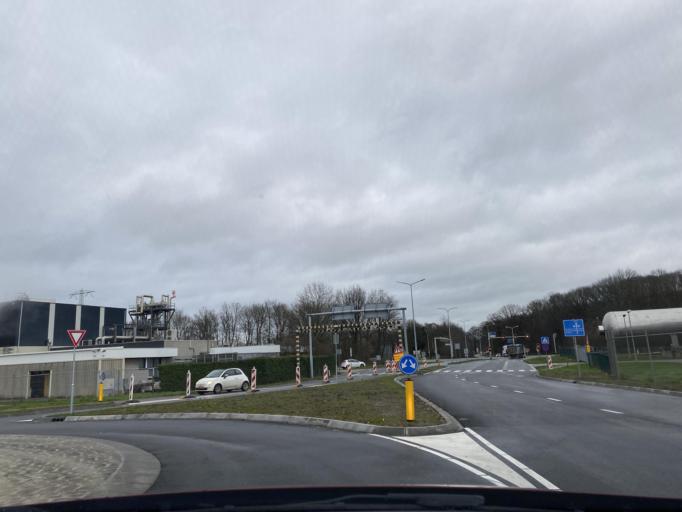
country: NL
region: Limburg
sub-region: Gemeente Stein
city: Urmond
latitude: 50.9886
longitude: 5.7899
